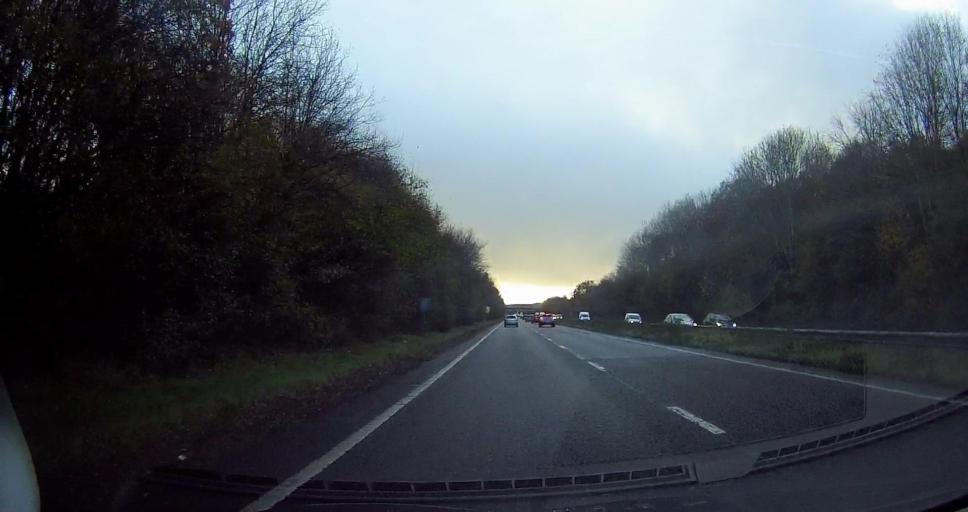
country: GB
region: England
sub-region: West Sussex
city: Hurstpierpoint
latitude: 50.9439
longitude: -0.1938
